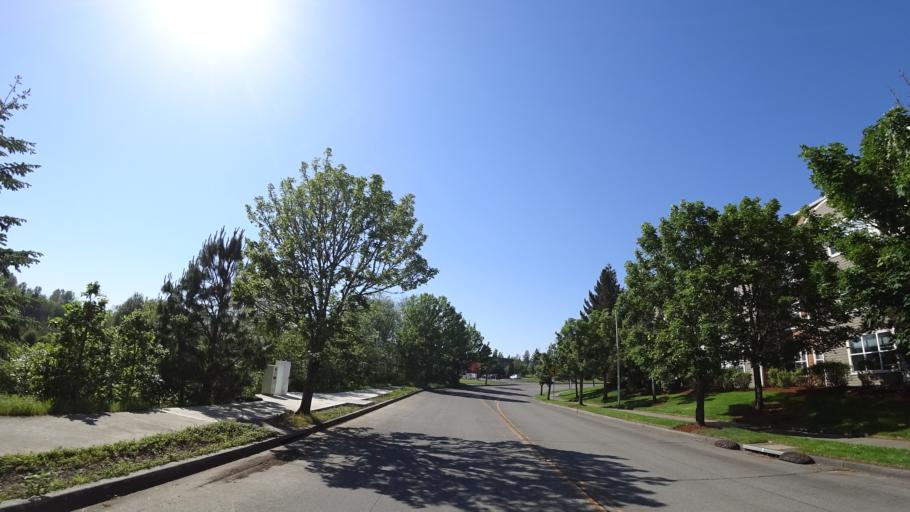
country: US
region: Oregon
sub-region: Washington County
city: Beaverton
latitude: 45.4936
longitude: -122.8335
